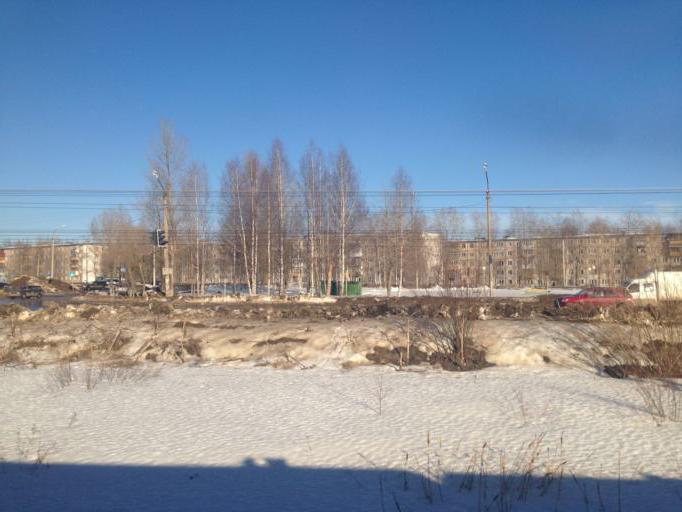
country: RU
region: Komi Republic
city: Ezhva
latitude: 61.7973
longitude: 50.7367
